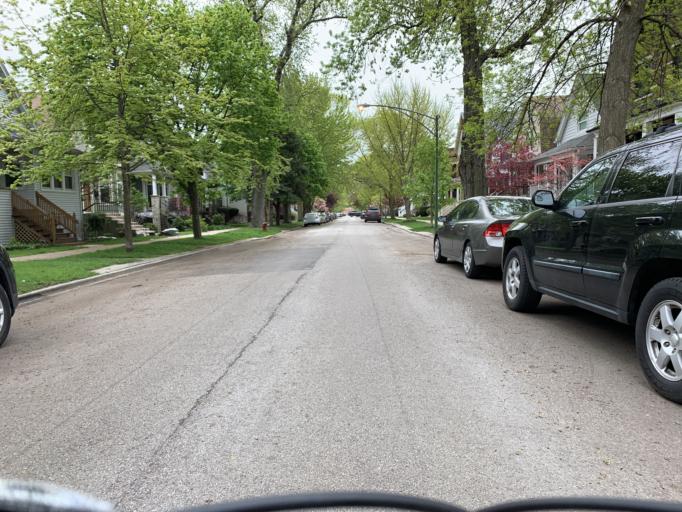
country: US
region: Illinois
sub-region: Cook County
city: Lincolnwood
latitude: 41.9718
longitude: -87.6831
